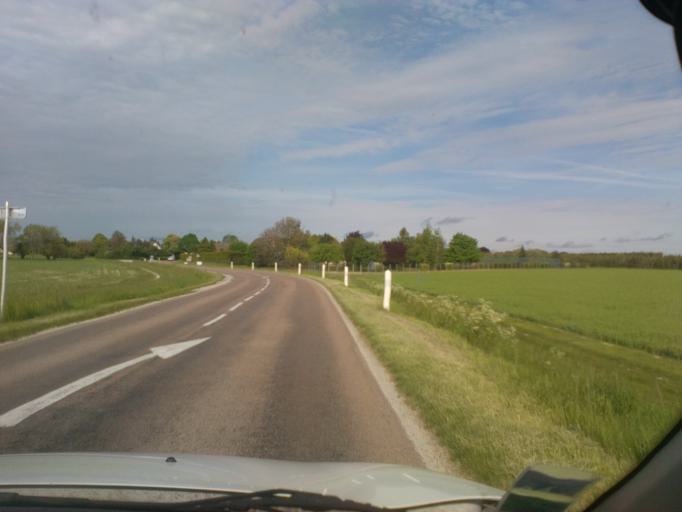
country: FR
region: Champagne-Ardenne
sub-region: Departement de l'Aube
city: Payns
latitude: 48.3684
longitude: 3.9092
